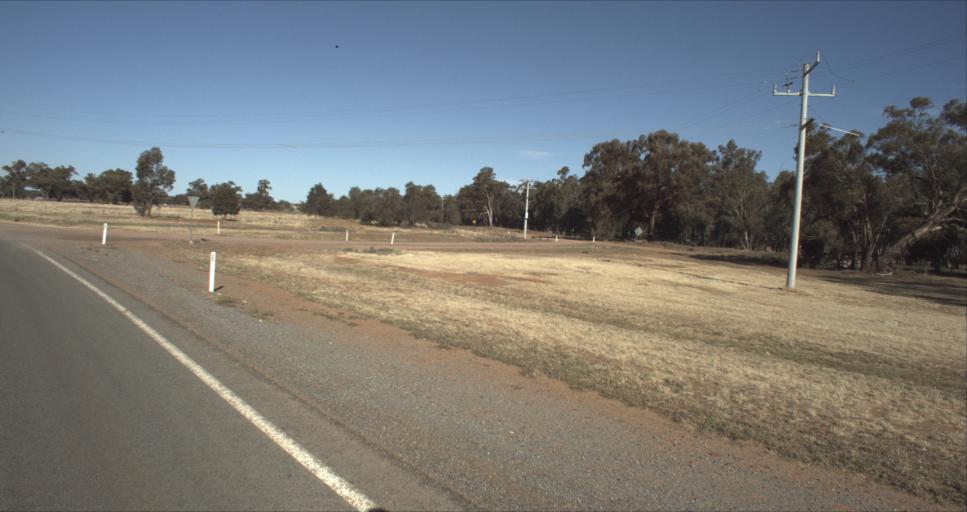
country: AU
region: New South Wales
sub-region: Leeton
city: Leeton
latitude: -34.6258
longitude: 146.3932
